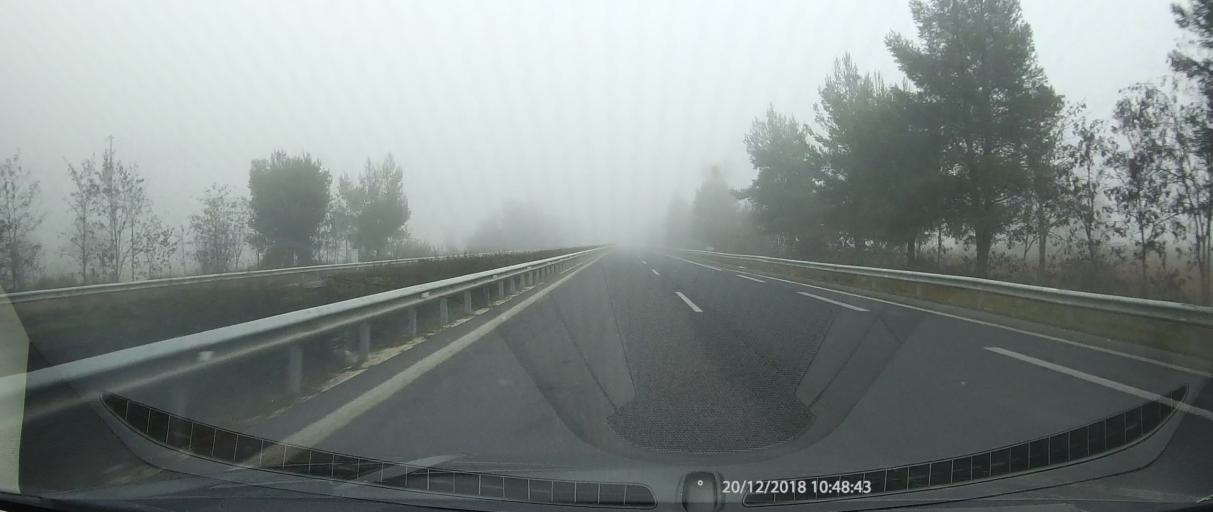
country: GR
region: Peloponnese
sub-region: Nomos Arkadias
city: Tripoli
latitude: 37.5227
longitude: 22.4084
